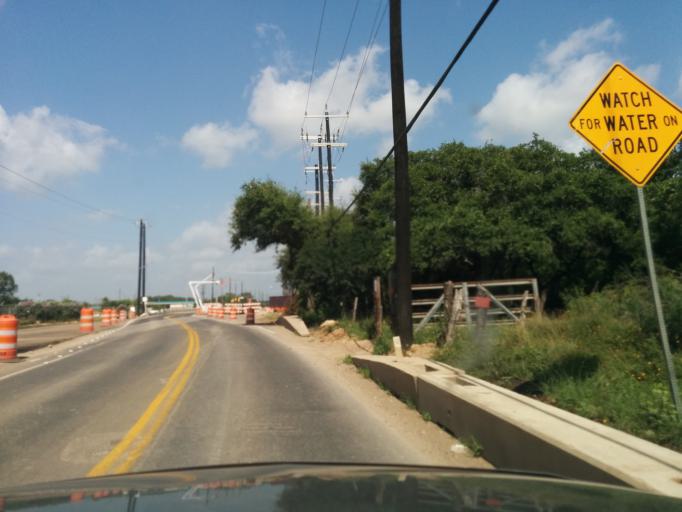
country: US
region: Texas
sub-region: Bexar County
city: Helotes
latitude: 29.5722
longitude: -98.6289
